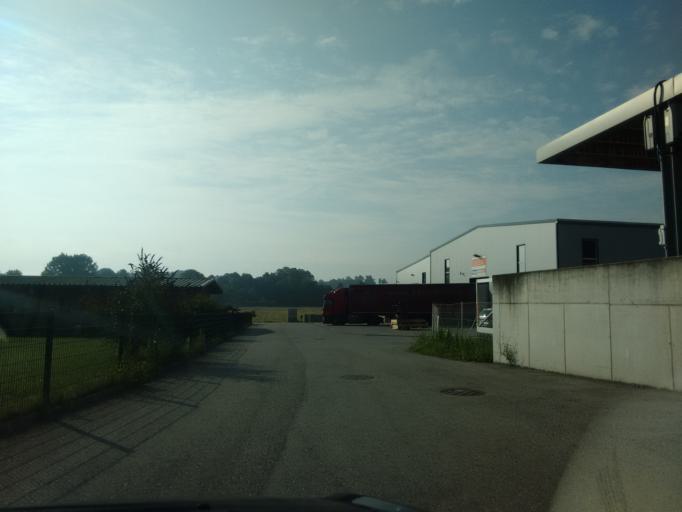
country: AT
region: Upper Austria
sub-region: Politischer Bezirk Grieskirchen
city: Bad Schallerbach
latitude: 48.2171
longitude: 13.9296
